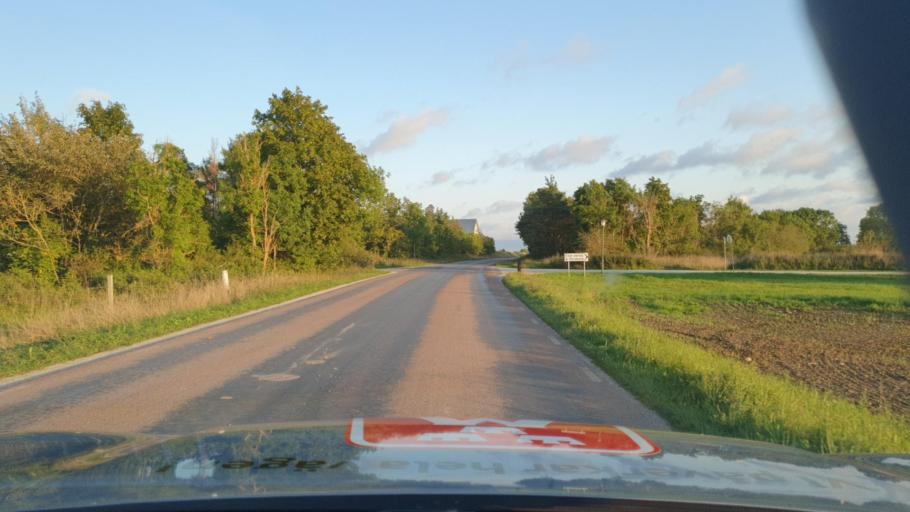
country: SE
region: Gotland
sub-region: Gotland
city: Visby
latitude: 57.6499
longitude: 18.5499
